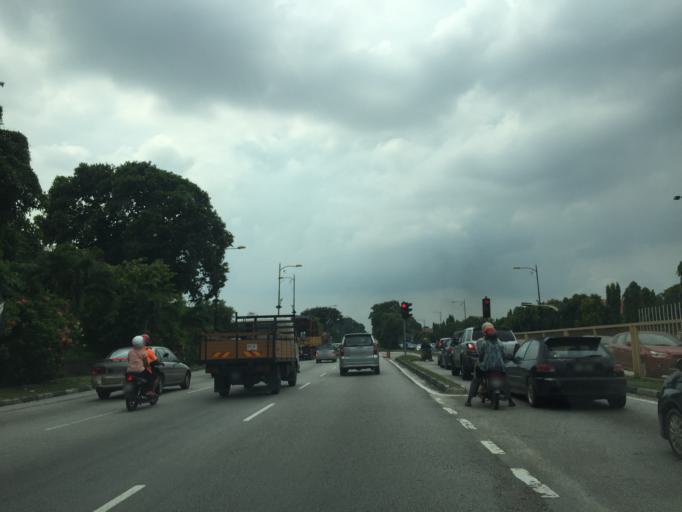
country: MY
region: Selangor
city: Klang
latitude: 3.0206
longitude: 101.4420
